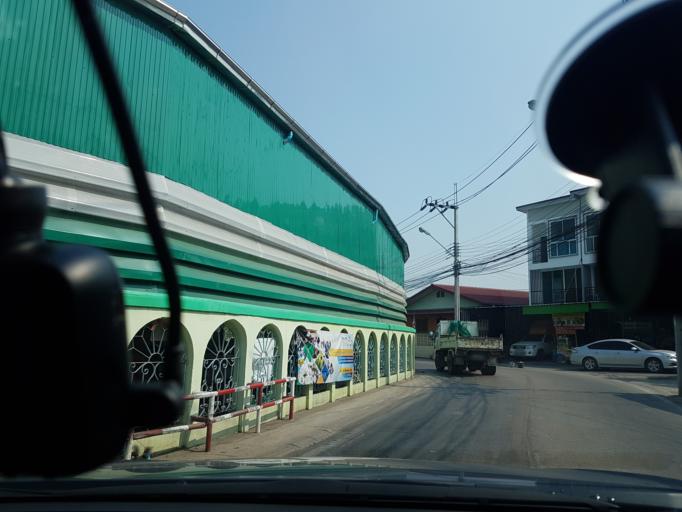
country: TH
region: Bangkok
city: Khlong Sam Wa
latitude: 13.8423
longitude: 100.7113
